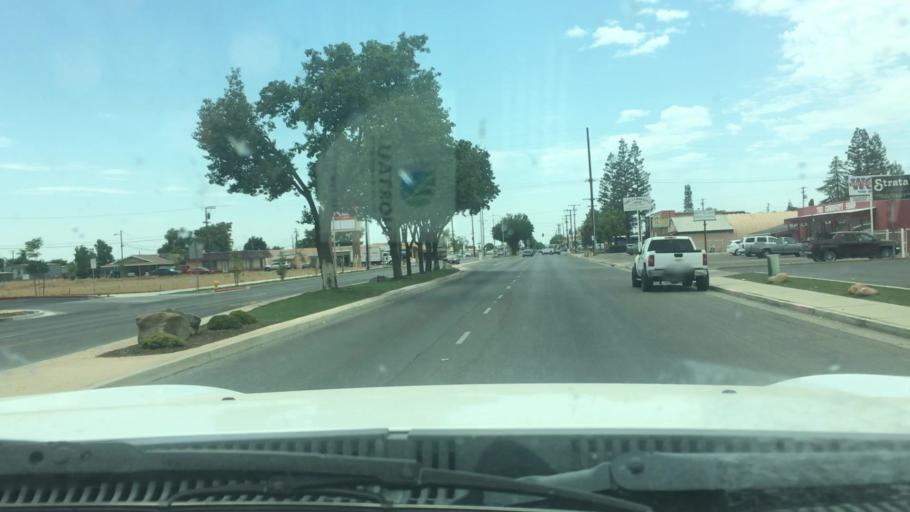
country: US
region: California
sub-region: Tulare County
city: Porterville
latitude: 36.0659
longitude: -119.0492
